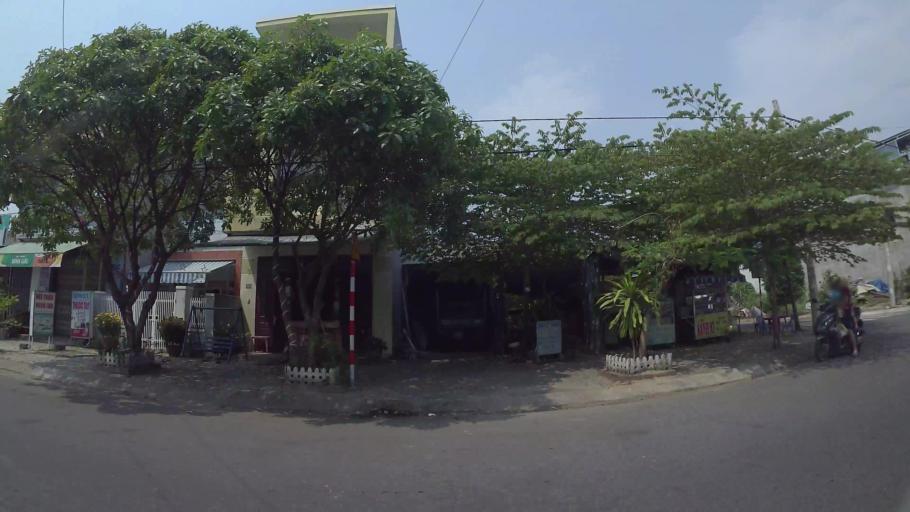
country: VN
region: Da Nang
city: Cam Le
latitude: 15.9920
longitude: 108.2136
